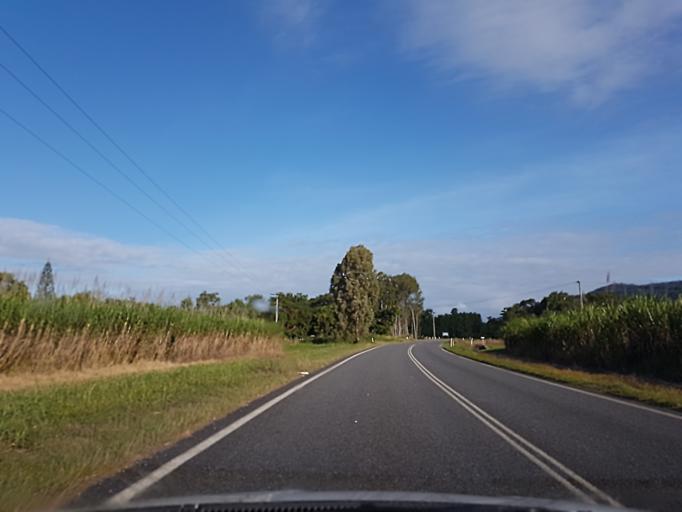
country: AU
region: Queensland
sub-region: Cairns
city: Port Douglas
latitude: -16.3354
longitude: 145.4104
